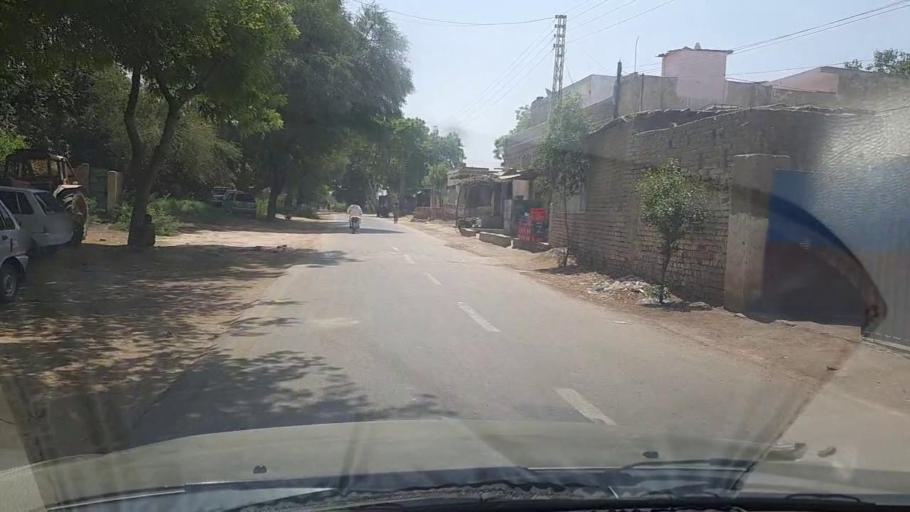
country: PK
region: Sindh
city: Tando Jam
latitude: 25.3414
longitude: 68.5215
